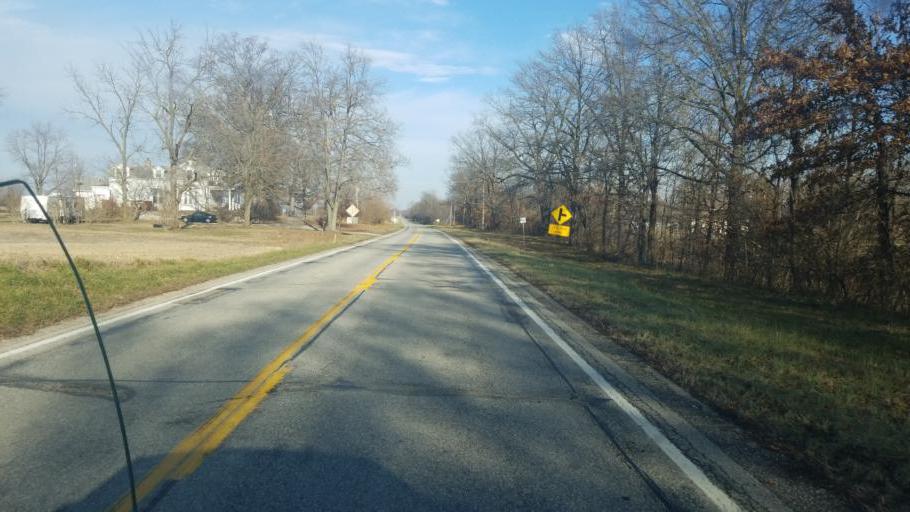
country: US
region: Illinois
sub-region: Wabash County
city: Mount Carmel
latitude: 38.3511
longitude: -87.8697
